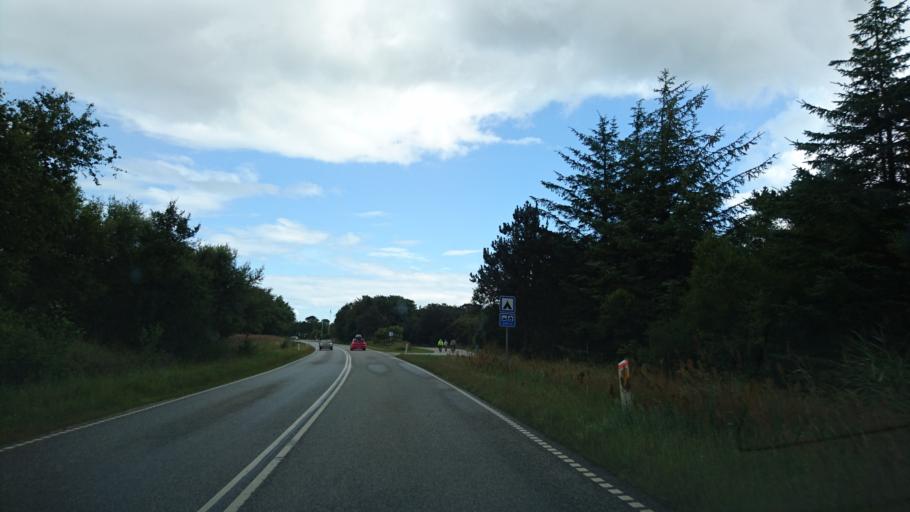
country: DK
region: North Denmark
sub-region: Frederikshavn Kommune
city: Skagen
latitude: 57.6421
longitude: 10.4604
